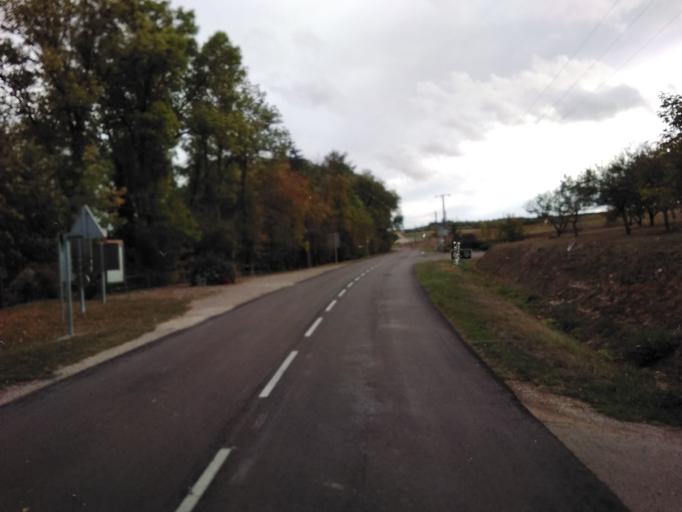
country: FR
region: Champagne-Ardenne
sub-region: Departement de l'Aube
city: Les Riceys
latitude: 47.9793
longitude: 4.3587
